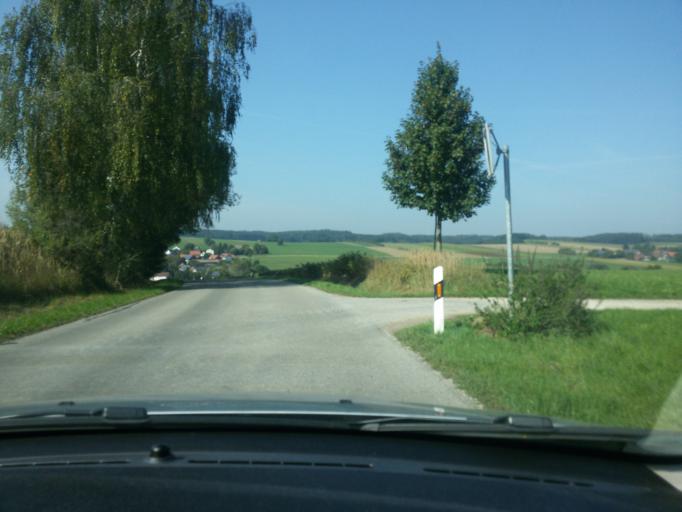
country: DE
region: Bavaria
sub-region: Swabia
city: Scherstetten
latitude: 48.1834
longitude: 10.6510
